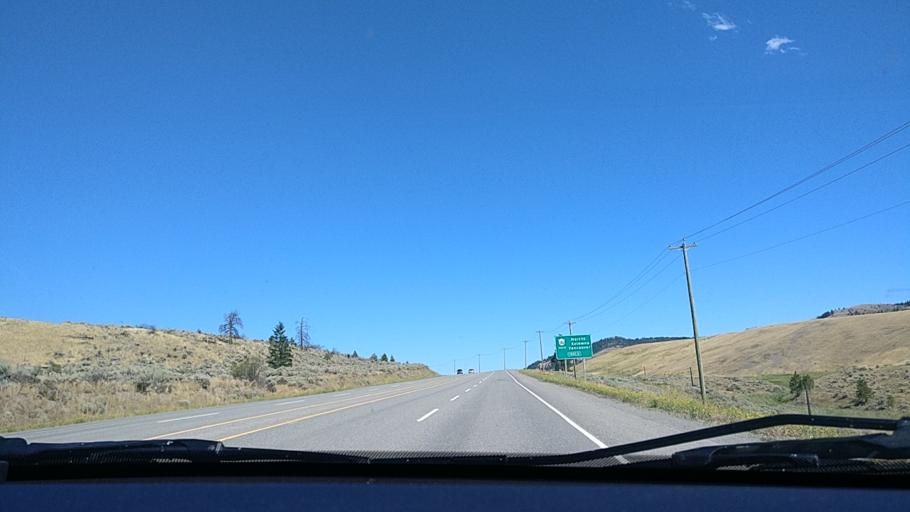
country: CA
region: British Columbia
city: Kamloops
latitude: 50.6692
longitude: -120.4801
